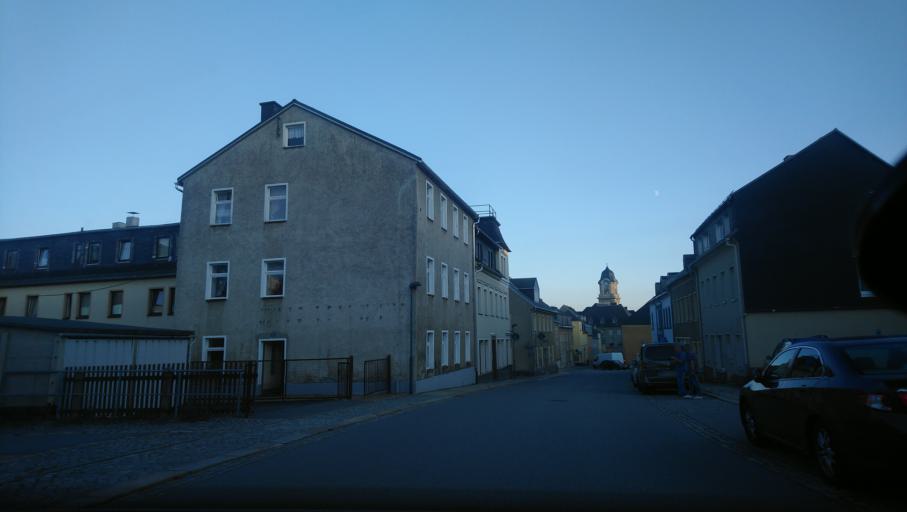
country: DE
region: Saxony
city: Geyer
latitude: 50.6258
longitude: 12.9211
